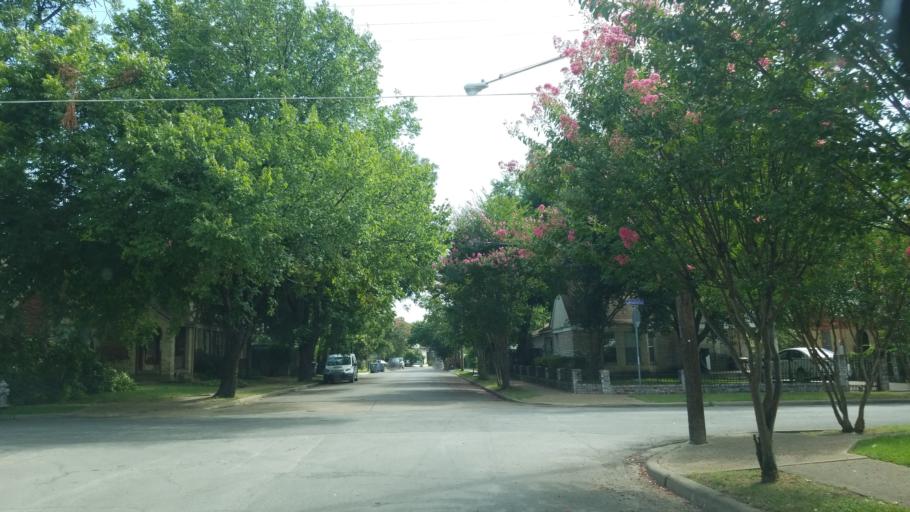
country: US
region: Texas
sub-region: Dallas County
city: Highland Park
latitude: 32.8171
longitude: -96.7797
